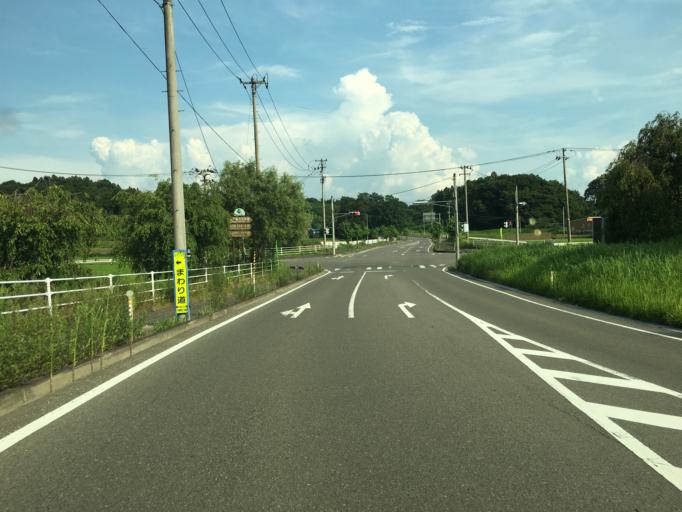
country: JP
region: Fukushima
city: Motomiya
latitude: 37.4907
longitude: 140.4269
